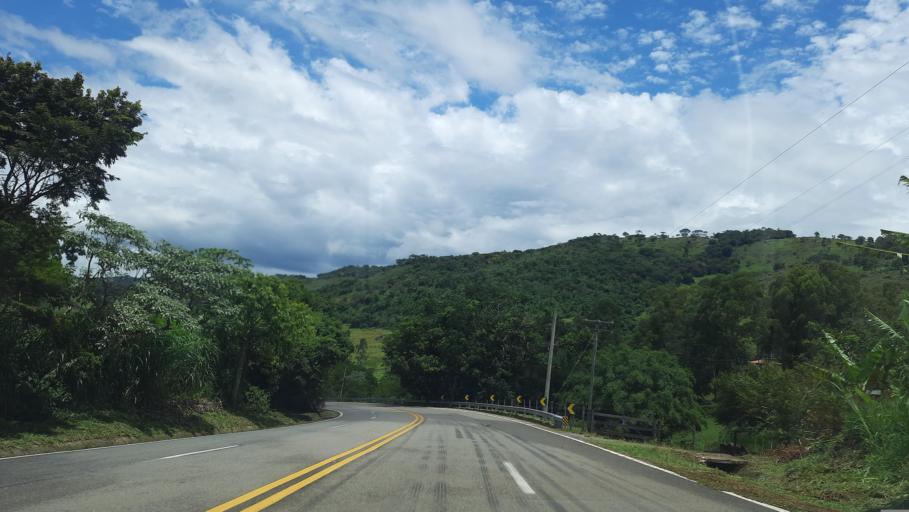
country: BR
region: Sao Paulo
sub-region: Vargem Grande Do Sul
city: Vargem Grande do Sul
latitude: -21.8258
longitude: -46.7783
